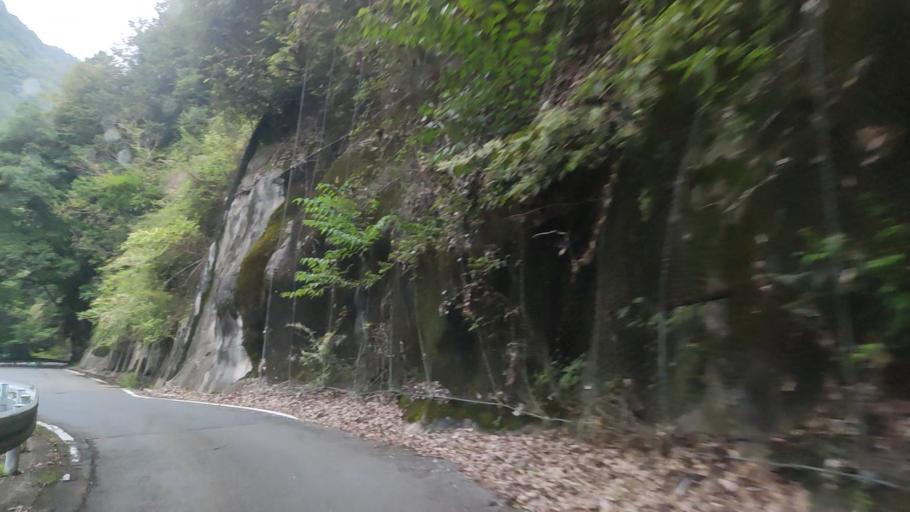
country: JP
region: Wakayama
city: Koya
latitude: 34.2562
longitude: 135.6526
